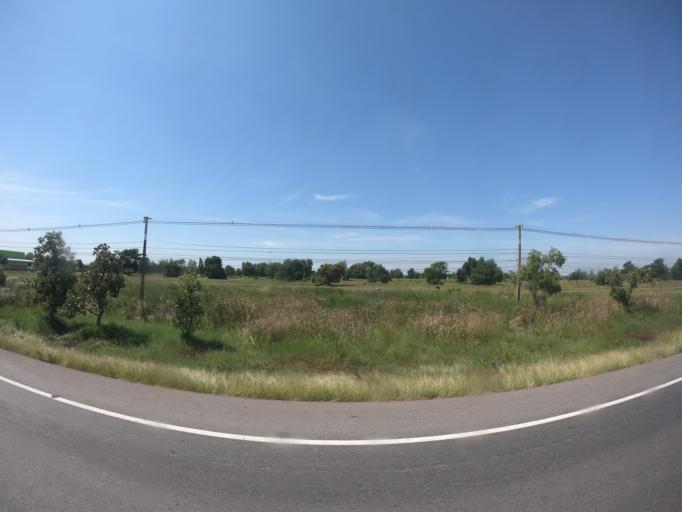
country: TH
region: Khon Kaen
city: Non Sila
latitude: 16.0073
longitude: 102.7038
